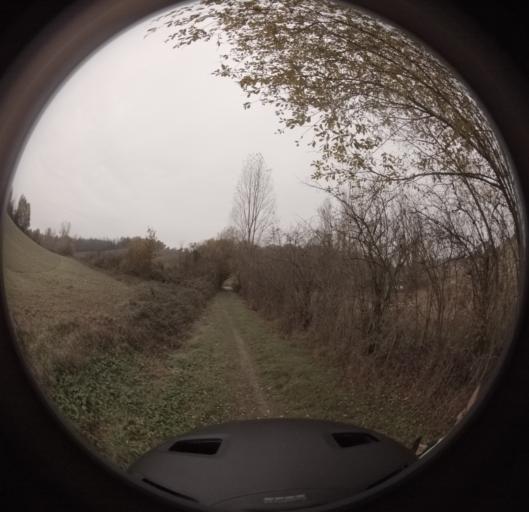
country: FR
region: Midi-Pyrenees
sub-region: Departement du Tarn-et-Garonne
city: Saint-Nauphary
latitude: 43.9739
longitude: 1.3918
